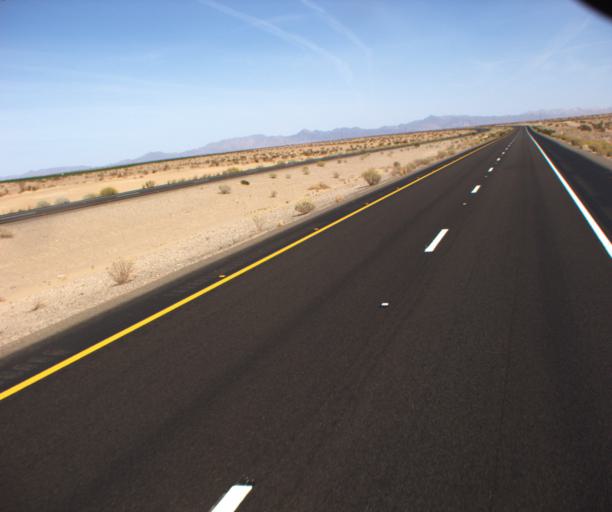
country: US
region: Arizona
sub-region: Yuma County
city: Somerton
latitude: 32.4951
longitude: -114.5759
